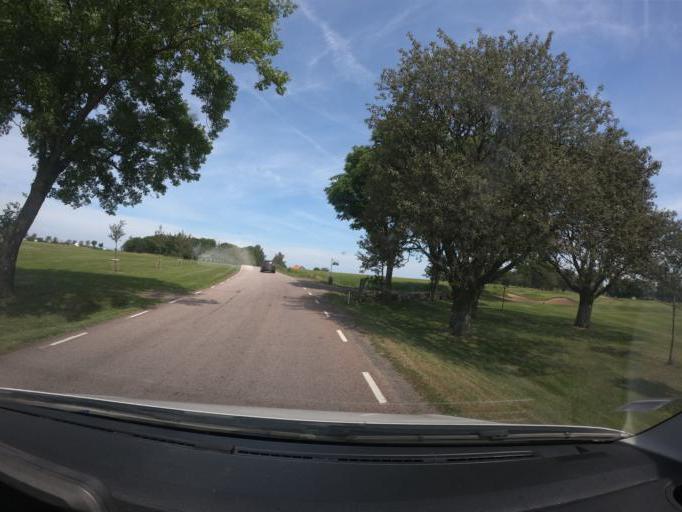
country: SE
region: Skane
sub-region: Bastads Kommun
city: Bastad
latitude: 56.4307
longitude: 12.7910
